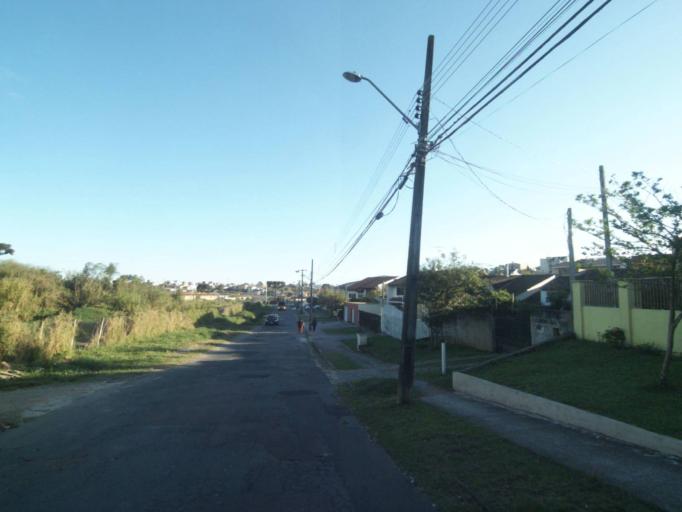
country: BR
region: Parana
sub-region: Curitiba
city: Curitiba
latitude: -25.3770
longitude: -49.2492
